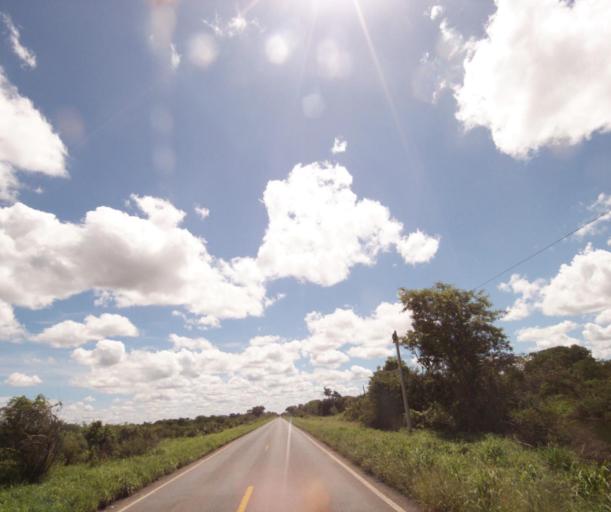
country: BR
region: Bahia
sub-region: Sao Felix Do Coribe
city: Santa Maria da Vitoria
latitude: -13.3900
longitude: -44.1054
